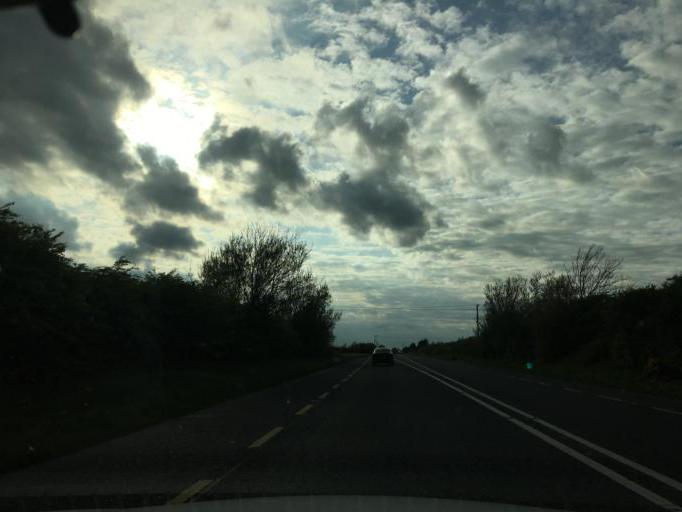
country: IE
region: Leinster
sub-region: Loch Garman
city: Loch Garman
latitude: 52.3418
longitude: -6.5751
